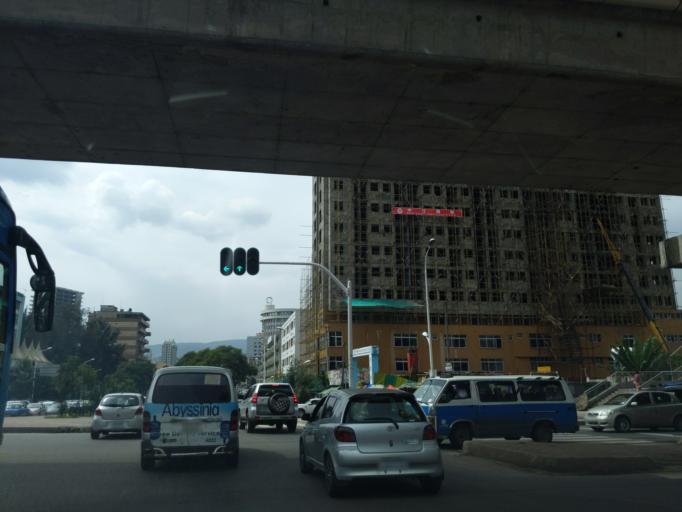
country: ET
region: Adis Abeba
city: Addis Ababa
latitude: 9.0117
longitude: 38.7533
